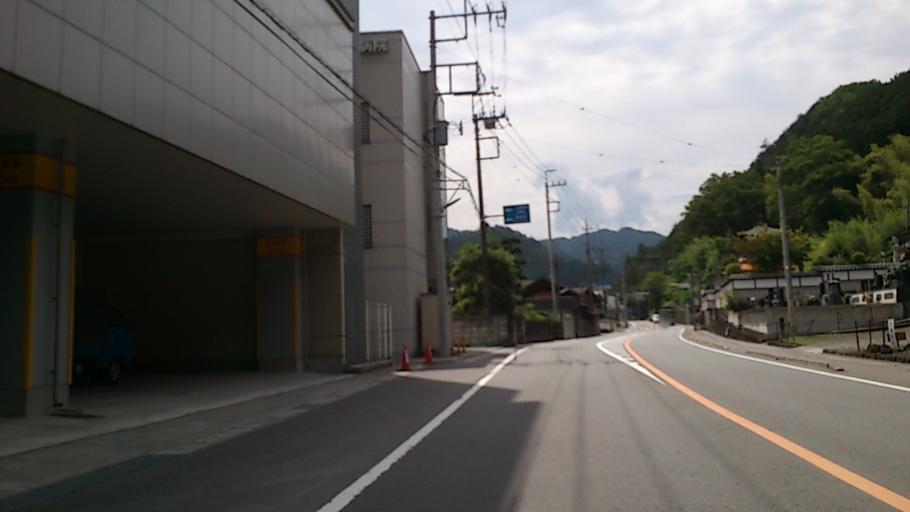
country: JP
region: Gunma
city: Tomioka
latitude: 36.2136
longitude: 138.7859
